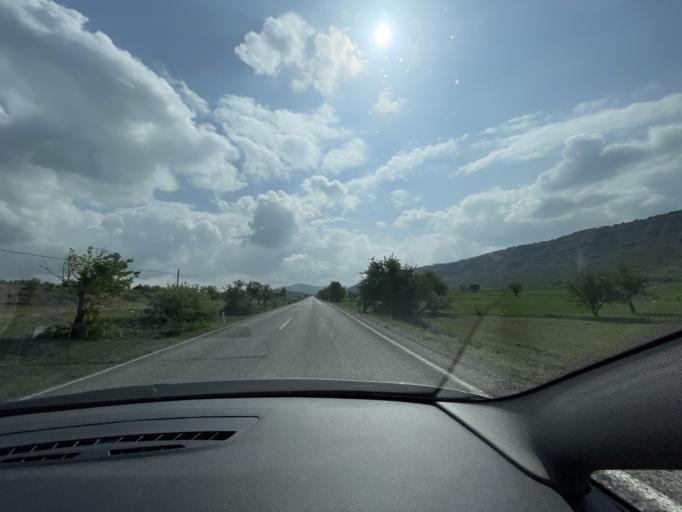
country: TR
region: Denizli
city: Acipayam
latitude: 37.5106
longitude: 29.4508
